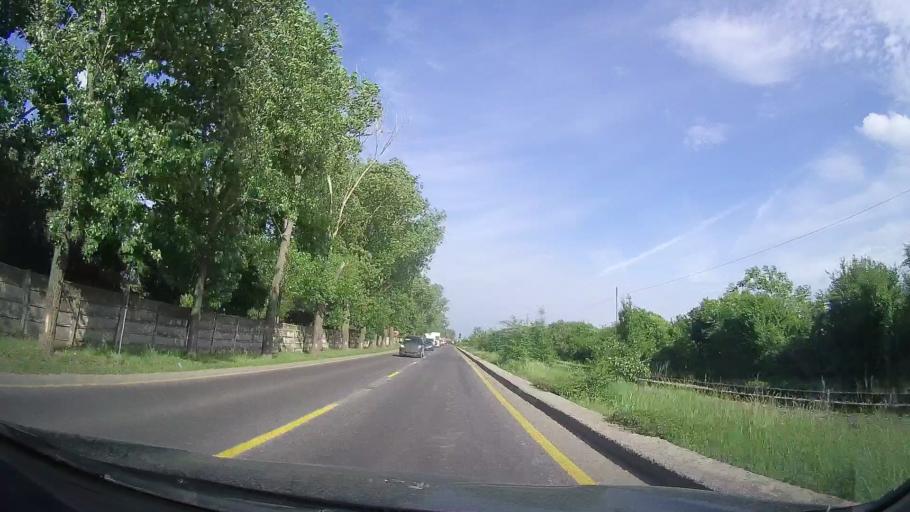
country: RO
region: Ilfov
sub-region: Comuna Magurele
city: Magurele
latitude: 44.3639
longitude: 26.0232
